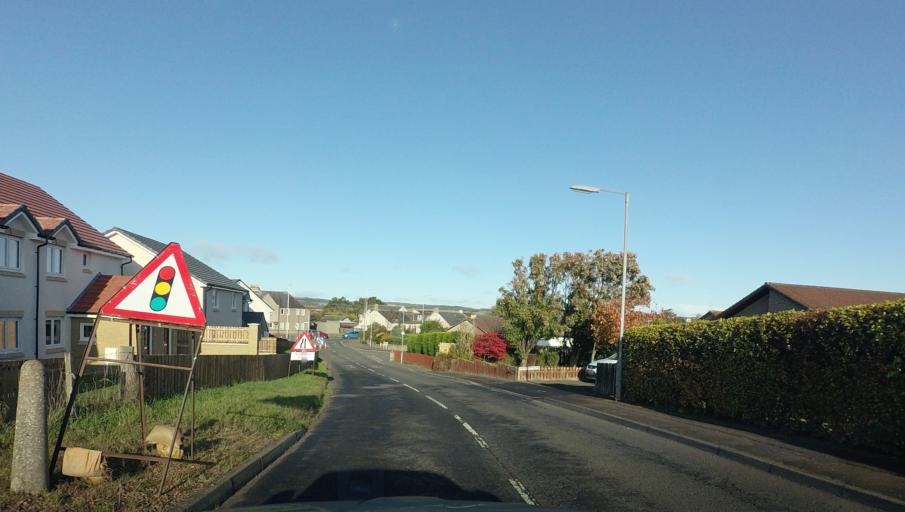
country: GB
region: Scotland
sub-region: Fife
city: Townhill
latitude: 56.0957
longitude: -3.4071
